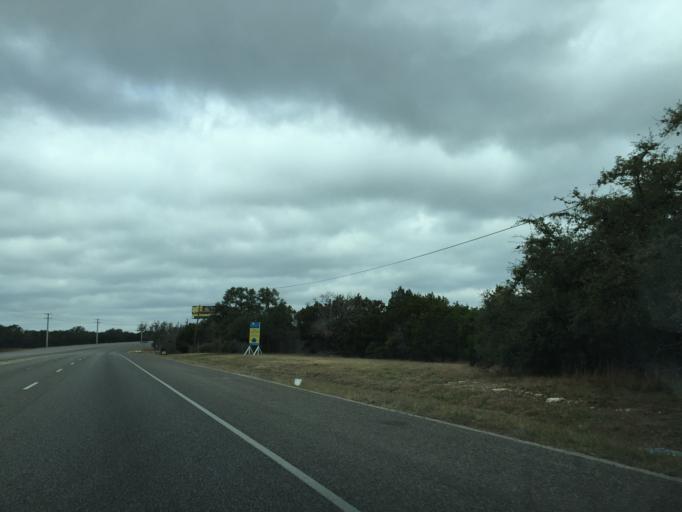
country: US
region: Texas
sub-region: Travis County
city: Briarcliff
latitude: 30.3479
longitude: -98.0563
